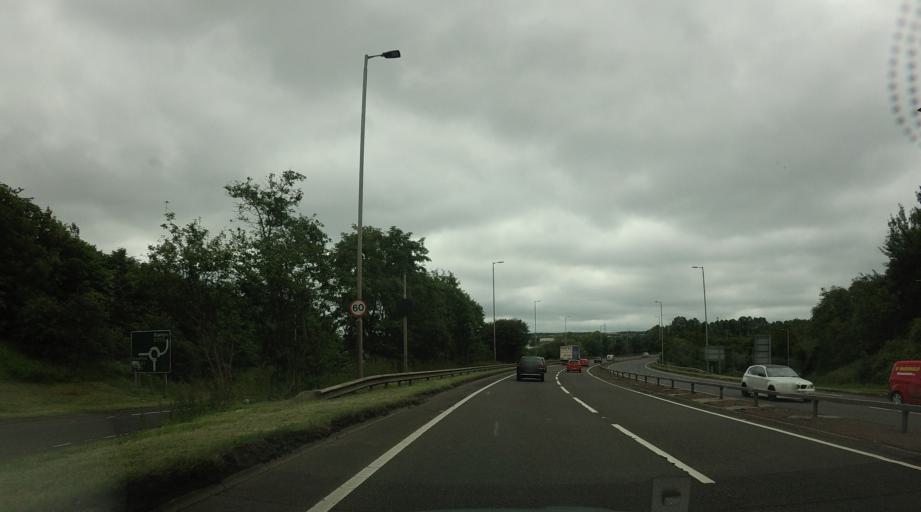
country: GB
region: Scotland
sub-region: South Lanarkshire
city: High Blantyre
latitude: 55.7862
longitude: -4.0865
